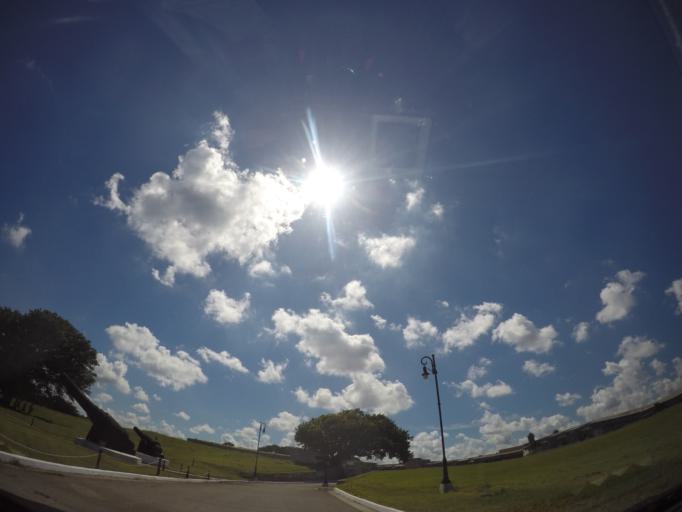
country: CU
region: La Habana
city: Centro Habana
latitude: 23.1489
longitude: -82.3510
